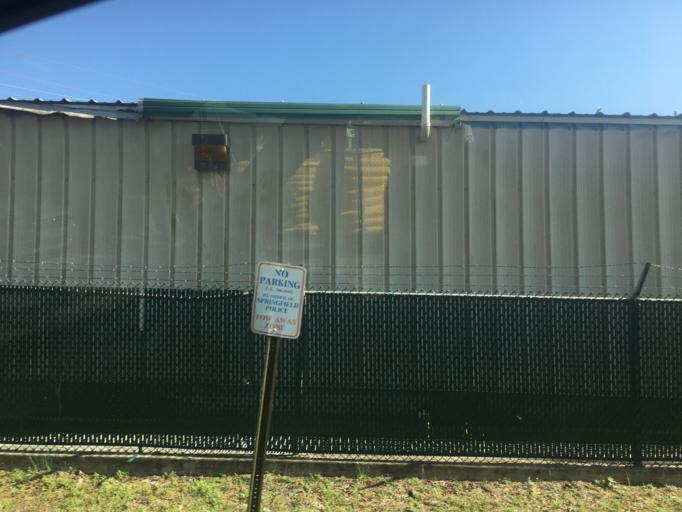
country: US
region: Florida
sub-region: Bay County
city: Springfield
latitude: 30.1458
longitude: -85.6179
